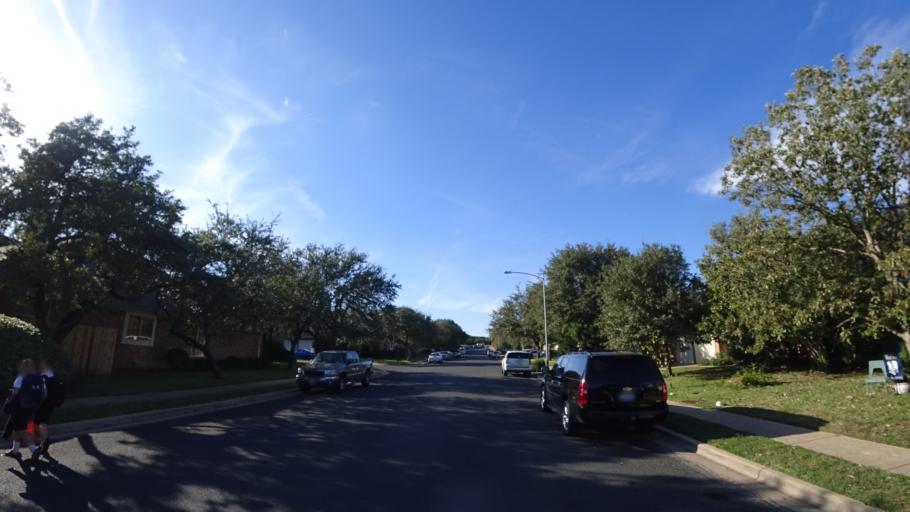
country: US
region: Texas
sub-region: Travis County
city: Barton Creek
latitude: 30.2523
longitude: -97.8441
